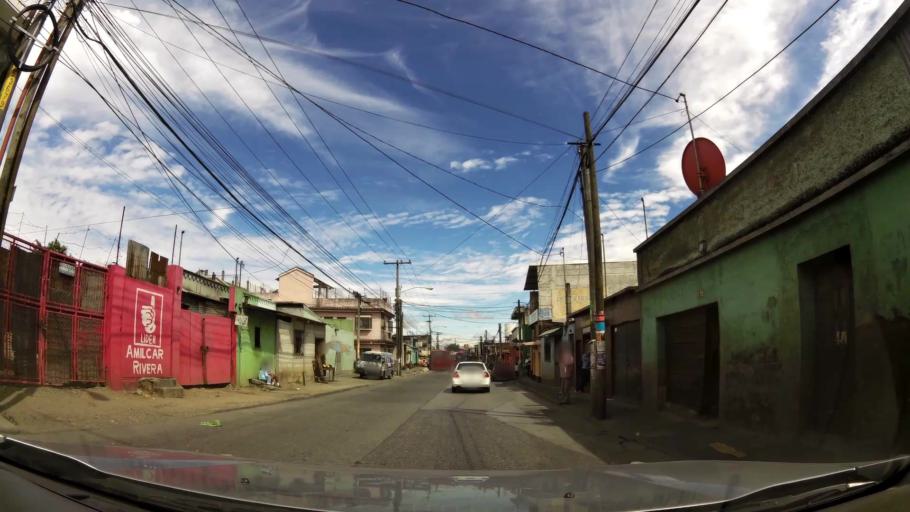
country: GT
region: Guatemala
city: Mixco
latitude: 14.6520
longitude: -90.5883
